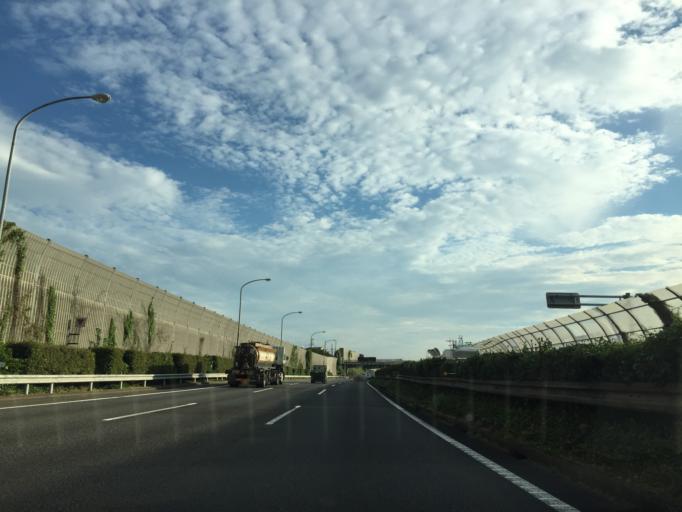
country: JP
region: Kanagawa
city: Minami-rinkan
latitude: 35.4536
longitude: 139.4267
